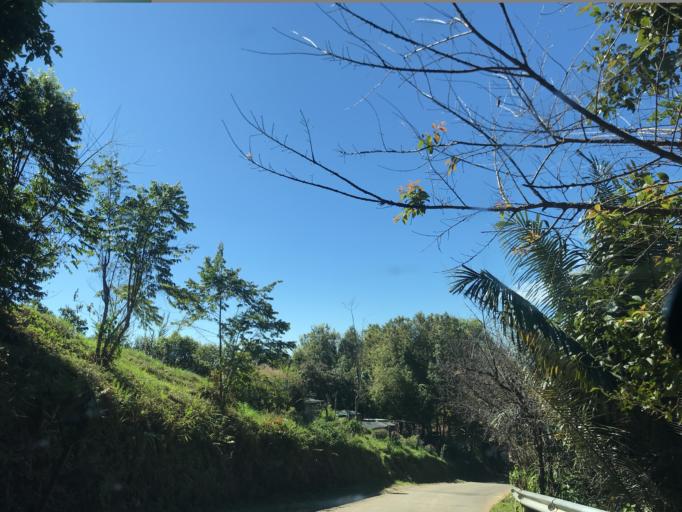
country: TH
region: Chiang Rai
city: Mae Lao
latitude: 19.8183
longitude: 99.5713
